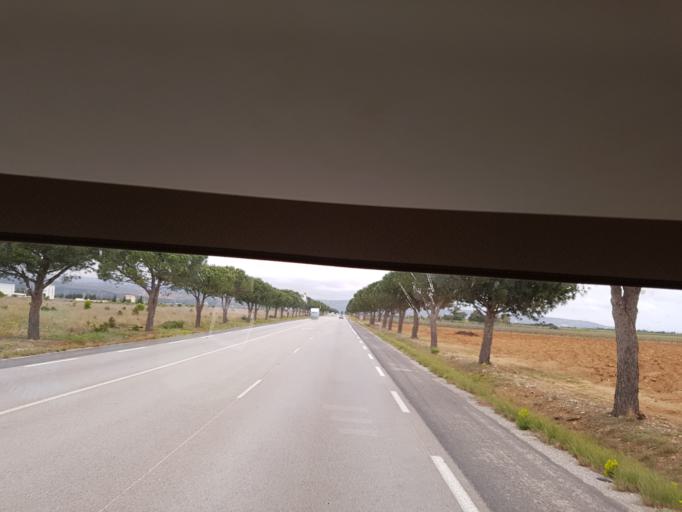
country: FR
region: Languedoc-Roussillon
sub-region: Departement des Pyrenees-Orientales
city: Salses-le-Chateau
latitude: 42.8049
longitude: 2.9115
